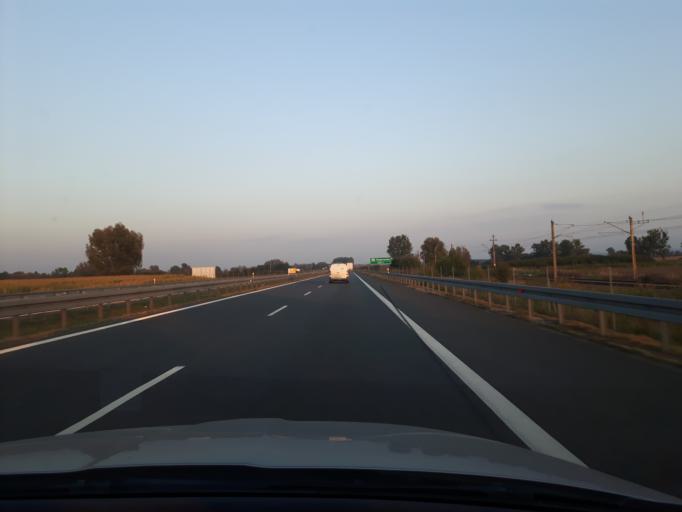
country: PL
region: Warmian-Masurian Voivodeship
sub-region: Powiat elblaski
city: Gronowo Gorne
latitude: 54.1034
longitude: 19.5205
